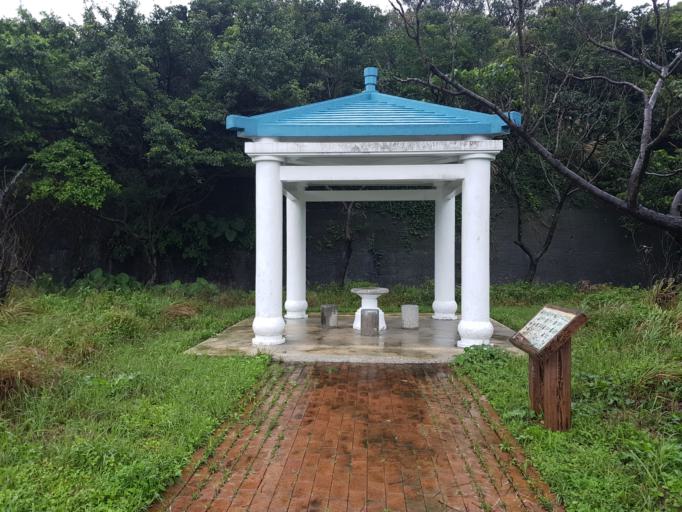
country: TW
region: Taiwan
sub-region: Keelung
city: Keelung
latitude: 25.1444
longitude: 121.7991
